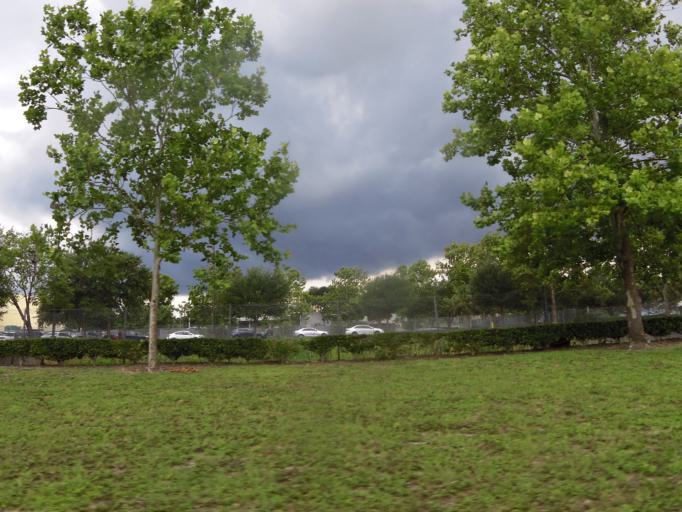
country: US
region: Florida
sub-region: Duval County
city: Jacksonville
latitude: 30.3260
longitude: -81.5435
